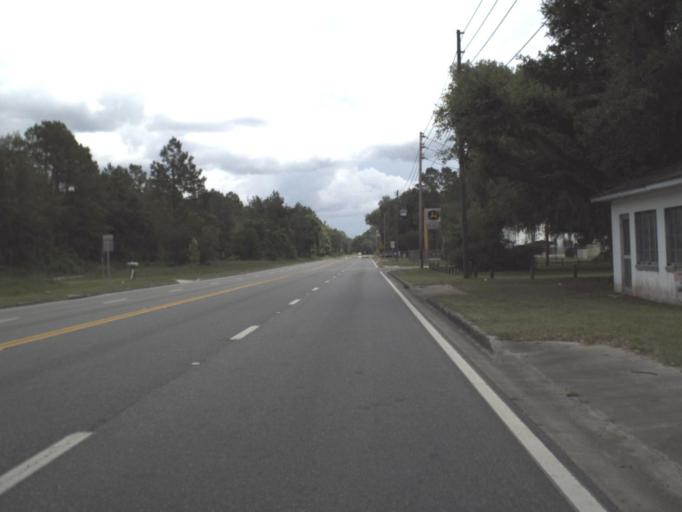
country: US
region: Florida
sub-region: Taylor County
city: Perry
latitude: 30.0918
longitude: -83.5385
